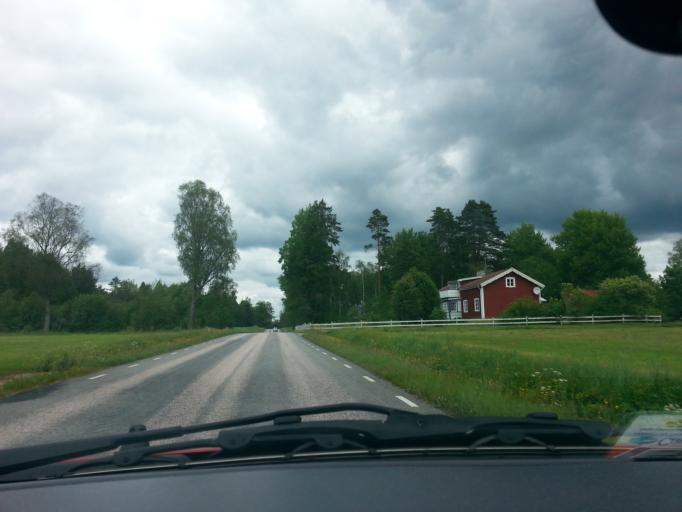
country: SE
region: Joenkoeping
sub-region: Gislaveds Kommun
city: Reftele
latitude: 57.1936
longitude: 13.5919
